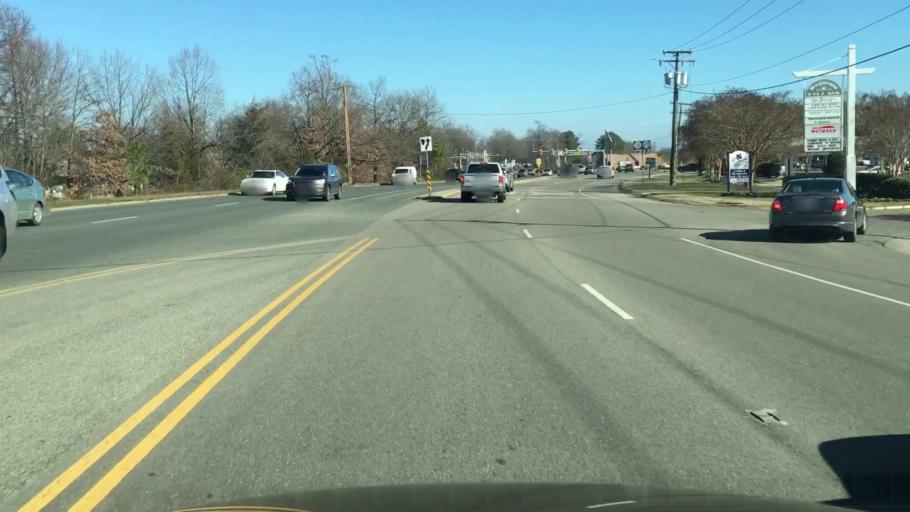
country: US
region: Virginia
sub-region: Chesterfield County
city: Bon Air
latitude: 37.5210
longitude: -77.6145
